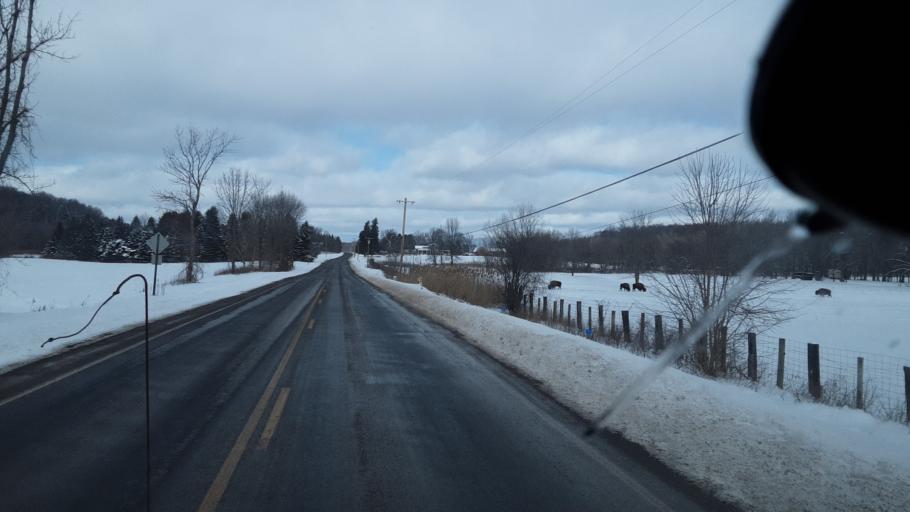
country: US
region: New York
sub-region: Wayne County
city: Newark
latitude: 43.0917
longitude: -77.0536
